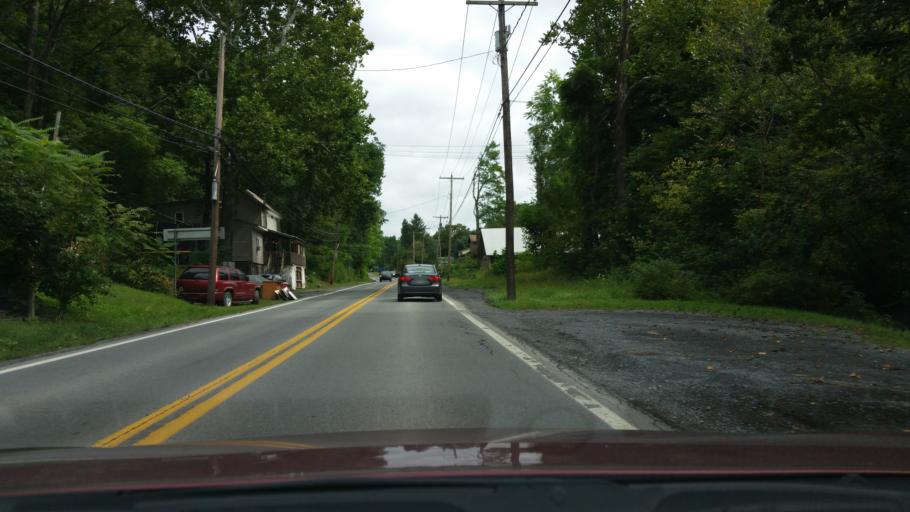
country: US
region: West Virginia
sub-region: Morgan County
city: Berkeley Springs
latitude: 39.6209
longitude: -78.2252
